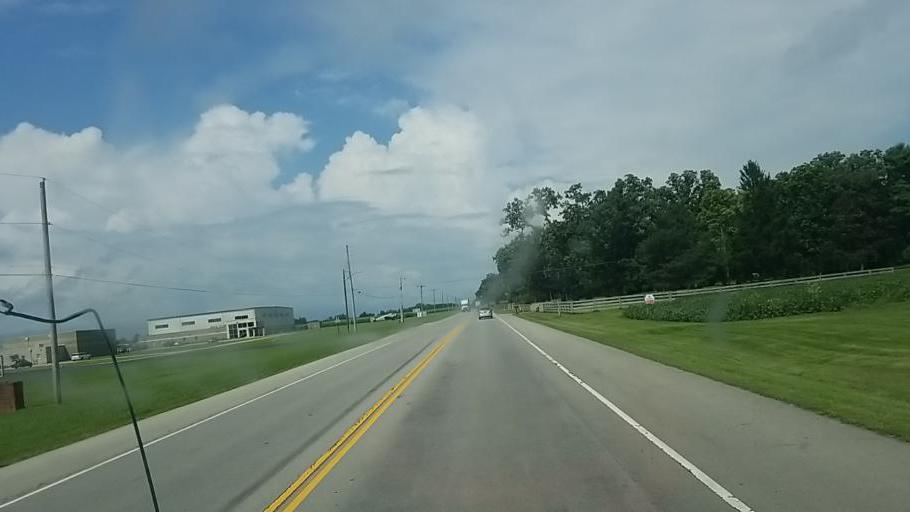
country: US
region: Ohio
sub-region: Champaign County
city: Urbana
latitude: 40.1324
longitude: -83.7481
